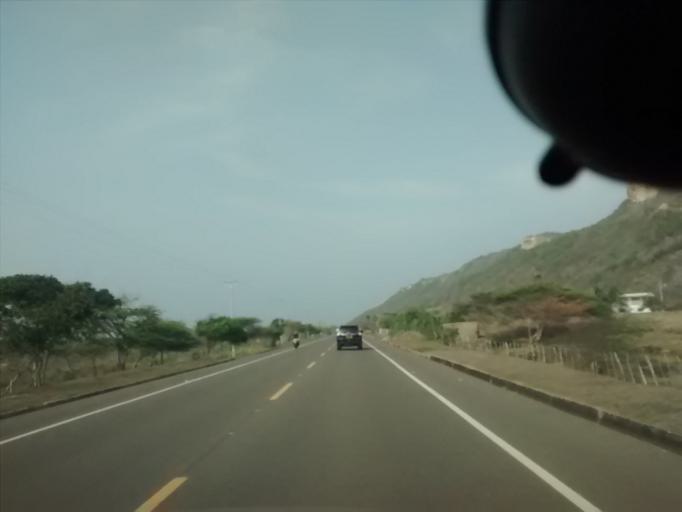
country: CO
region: Bolivar
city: Clemencia
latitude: 10.6231
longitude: -75.4440
